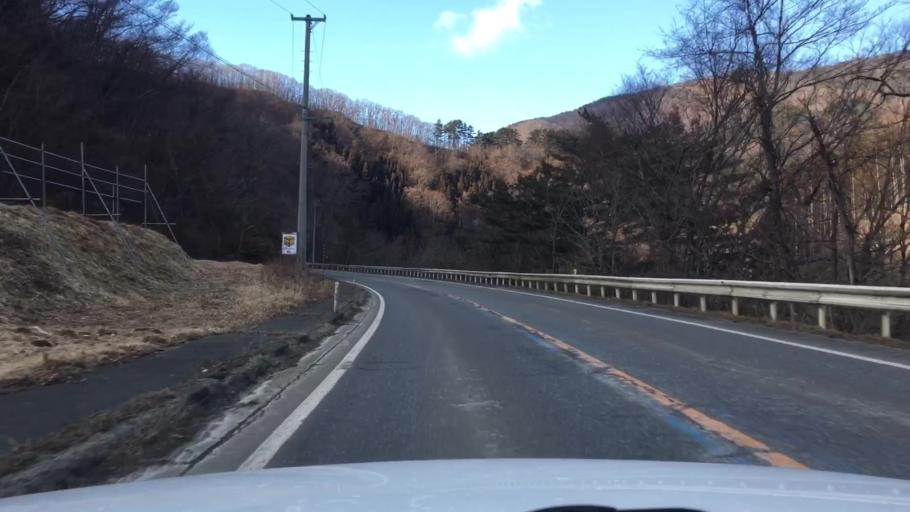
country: JP
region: Iwate
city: Tono
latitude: 39.6191
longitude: 141.6227
